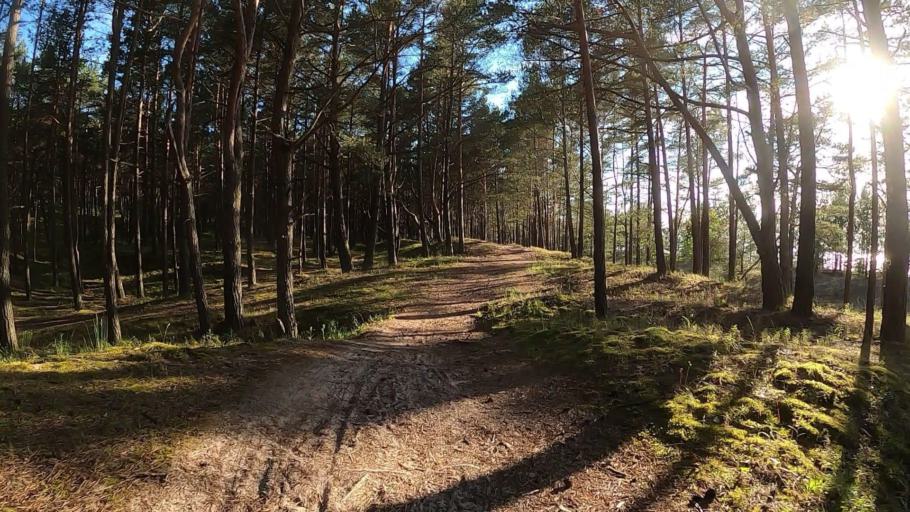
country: LV
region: Riga
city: Jaunciems
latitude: 57.0970
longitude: 24.1525
